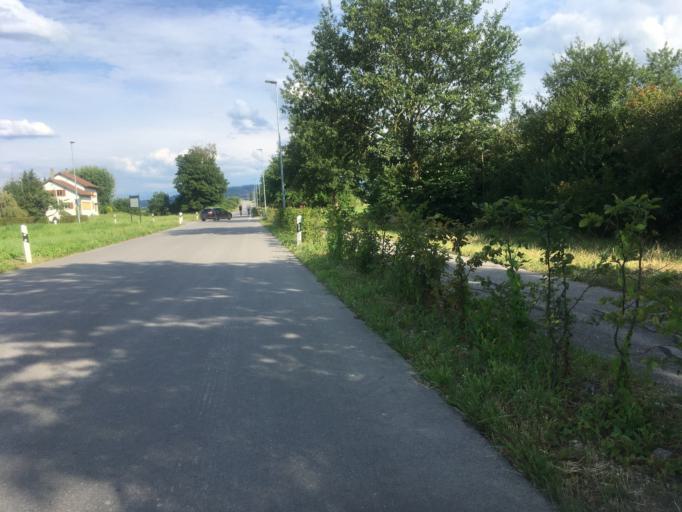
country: CH
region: Vaud
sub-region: Broye-Vully District
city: Payerne
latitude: 46.8373
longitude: 6.9129
